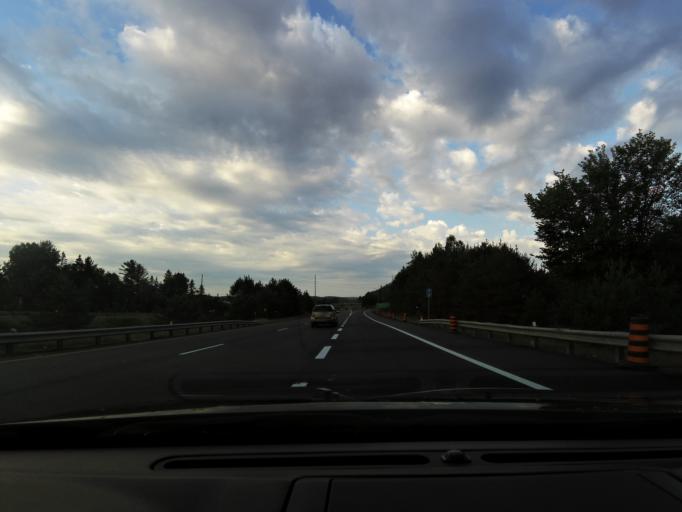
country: CA
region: Ontario
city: Huntsville
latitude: 45.3373
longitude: -79.2352
